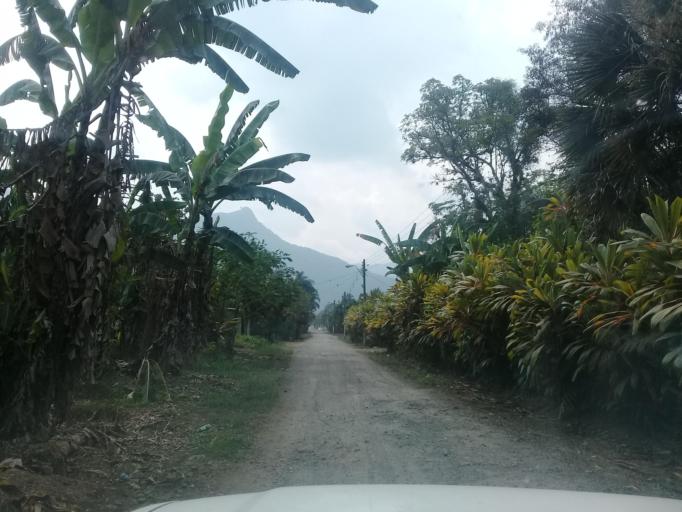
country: MX
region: Veracruz
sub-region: Ixtaczoquitlan
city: Capoluca
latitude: 18.8218
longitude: -96.9933
